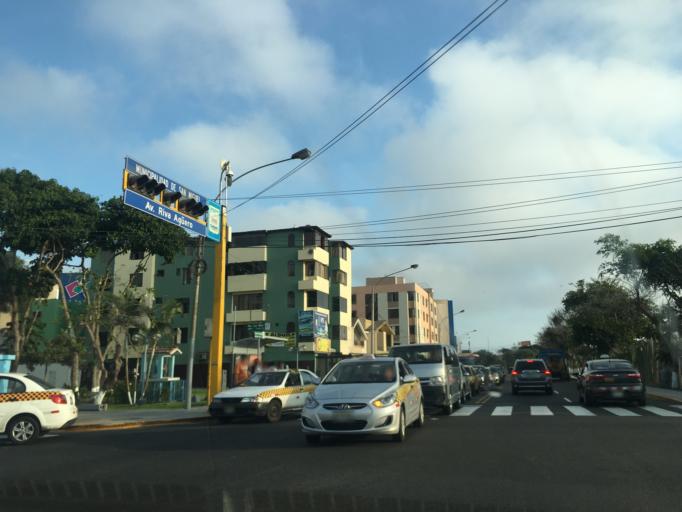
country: PE
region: Callao
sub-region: Callao
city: Callao
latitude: -12.0745
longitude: -77.0838
